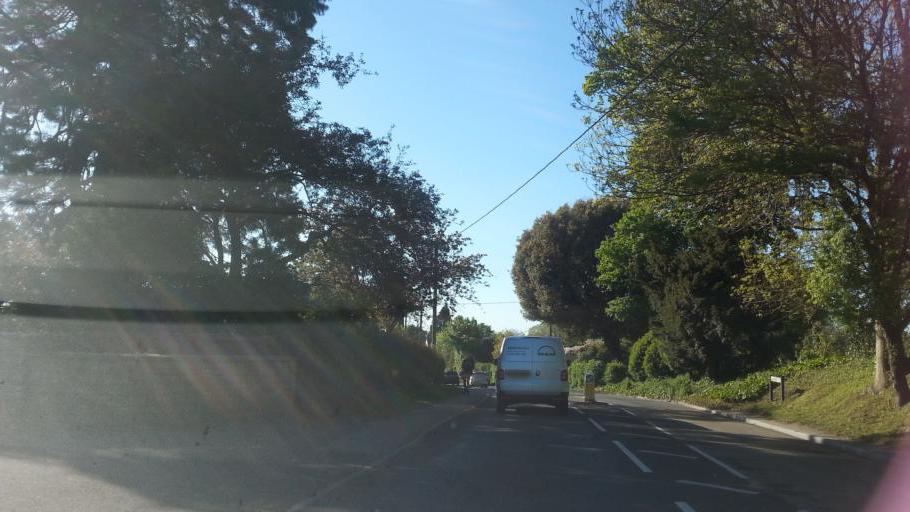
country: GB
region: England
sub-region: Somerset
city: Castle Cary
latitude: 51.0954
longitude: -2.5139
